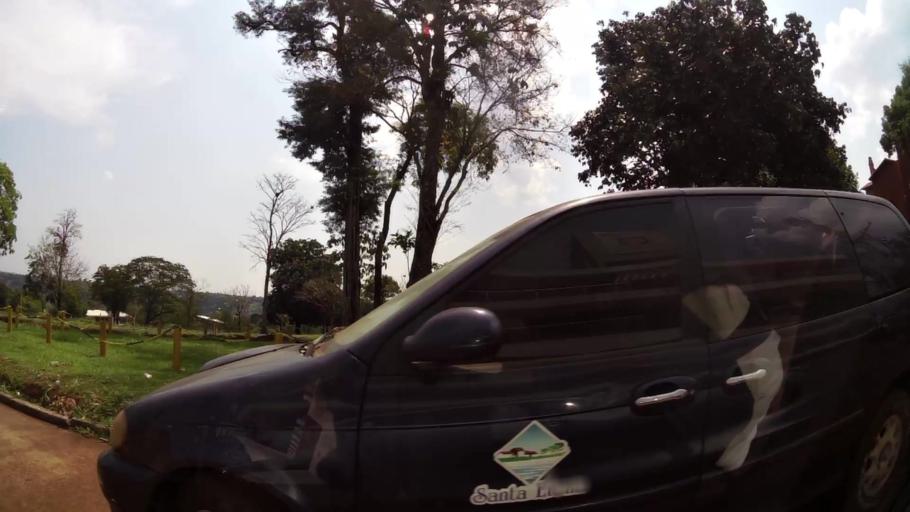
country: PY
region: Alto Parana
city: Ciudad del Este
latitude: -25.4826
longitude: -54.6248
